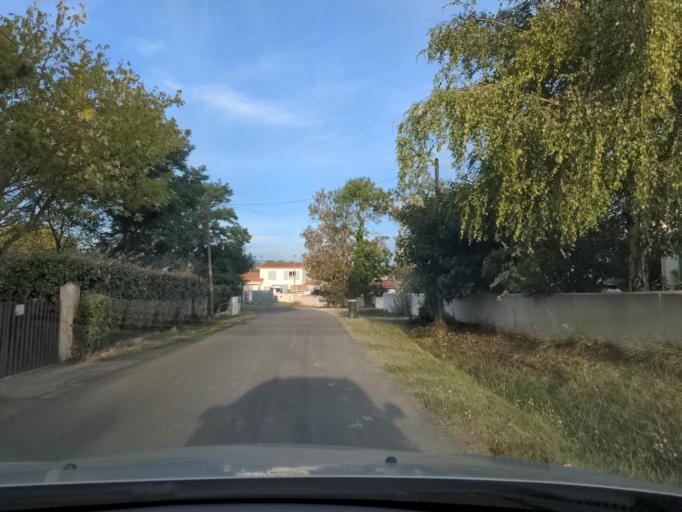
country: FR
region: Poitou-Charentes
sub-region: Departement de la Charente-Maritime
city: Saint-Trojan-les-Bains
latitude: 45.8862
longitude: -1.2087
